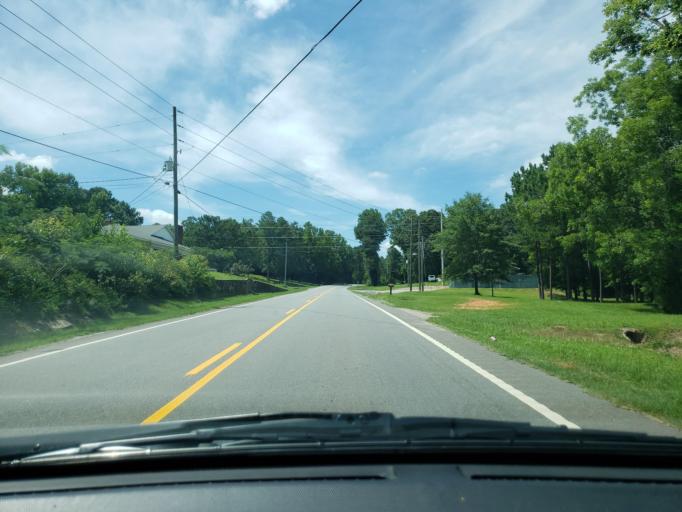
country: US
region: Alabama
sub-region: Elmore County
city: Eclectic
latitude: 32.6732
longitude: -85.9439
